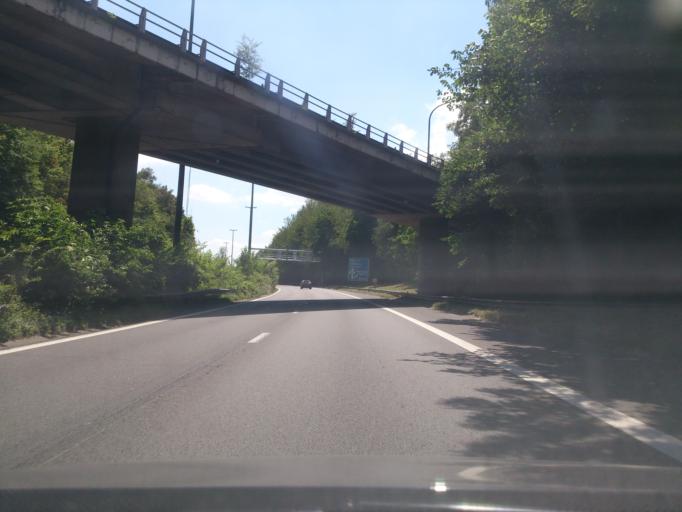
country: BE
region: Wallonia
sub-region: Province du Brabant Wallon
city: Waterloo
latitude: 50.7183
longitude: 4.4127
